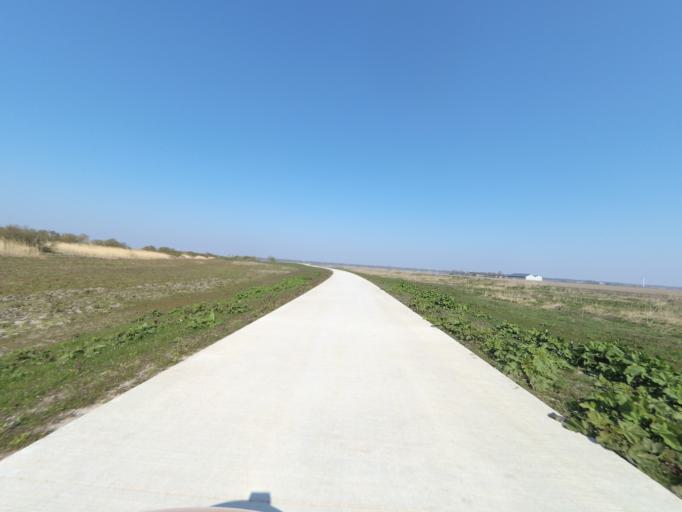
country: NL
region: Utrecht
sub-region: Gemeente Bunschoten
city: Spakenburg
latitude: 52.3530
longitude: 5.3956
